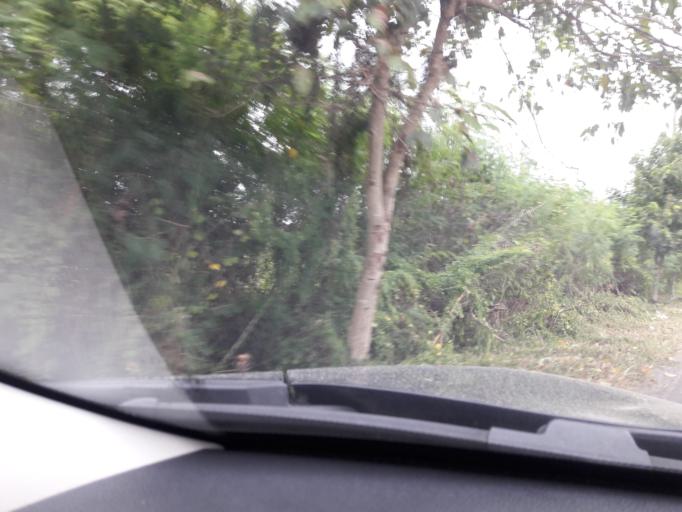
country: TH
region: Ratchaburi
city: Bang Phae
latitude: 13.6263
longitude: 99.9485
